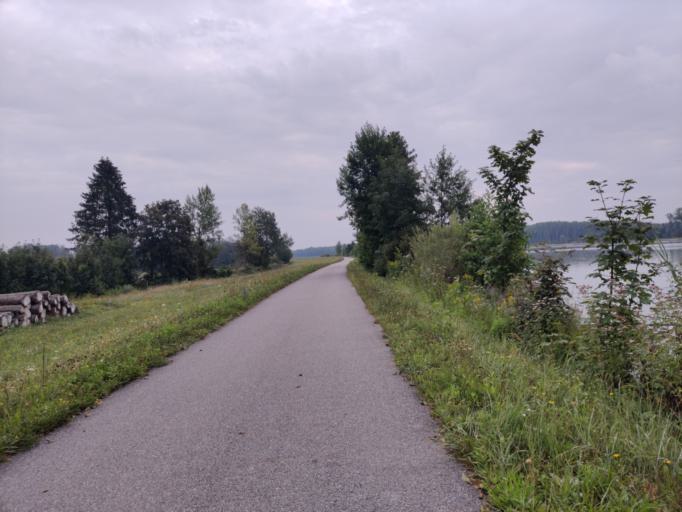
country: AT
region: Upper Austria
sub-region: Politischer Bezirk Urfahr-Umgebung
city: Steyregg
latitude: 48.2613
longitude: 14.3974
